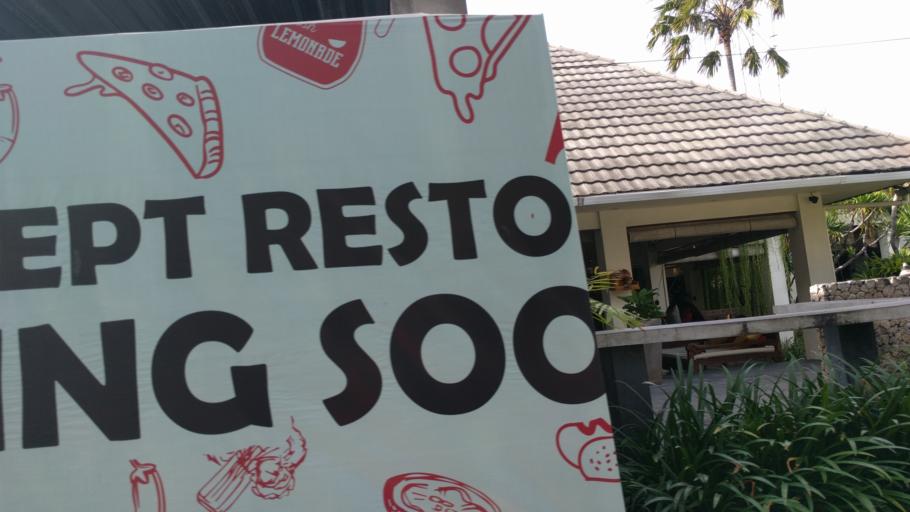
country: ID
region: Bali
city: Kuta
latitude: -8.6920
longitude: 115.1624
